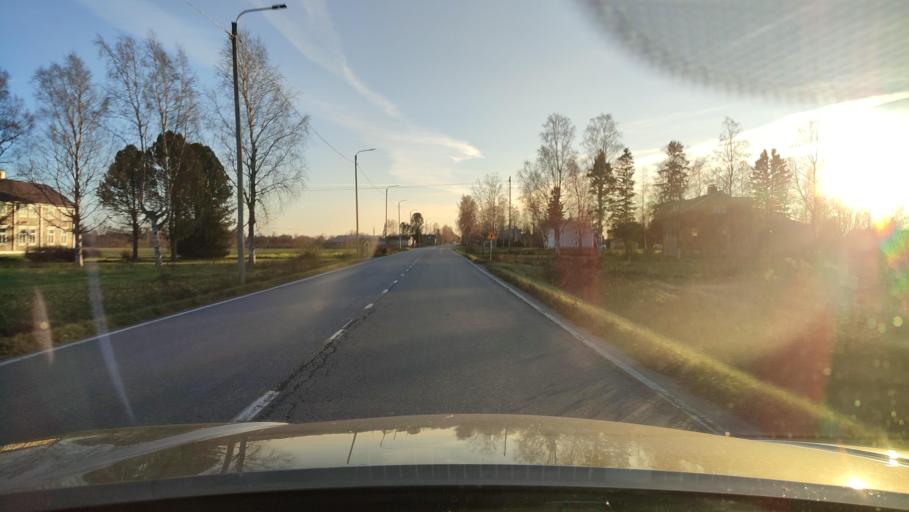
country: FI
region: Ostrobothnia
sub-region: Sydosterbotten
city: Naerpes
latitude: 62.6028
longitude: 21.4570
